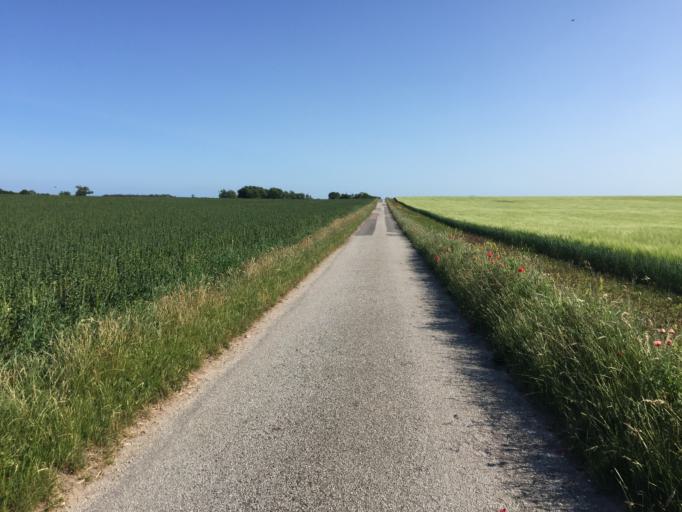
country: DK
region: Zealand
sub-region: Slagelse Kommune
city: Skaelskor
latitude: 55.2056
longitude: 11.1927
